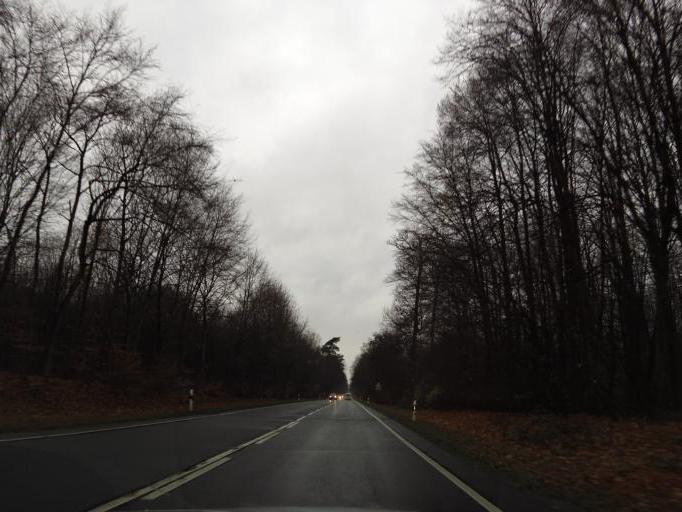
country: DE
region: Hesse
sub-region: Regierungsbezirk Darmstadt
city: Neu Isenburg
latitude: 50.0626
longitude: 8.6877
